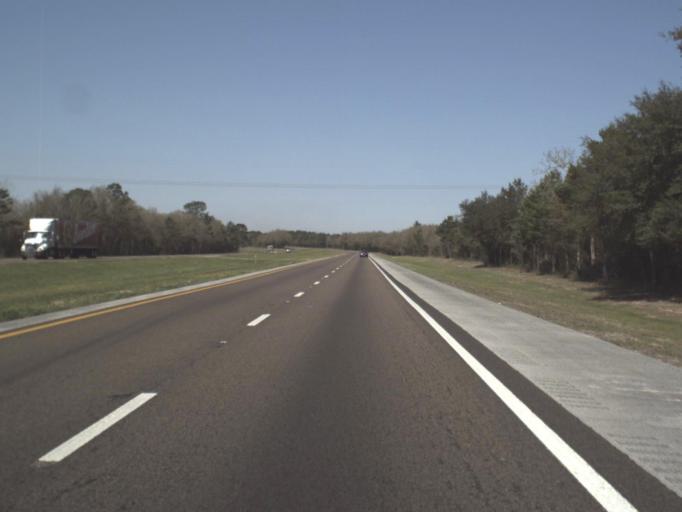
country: US
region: Florida
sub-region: Walton County
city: DeFuniak Springs
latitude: 30.7473
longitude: -86.2388
